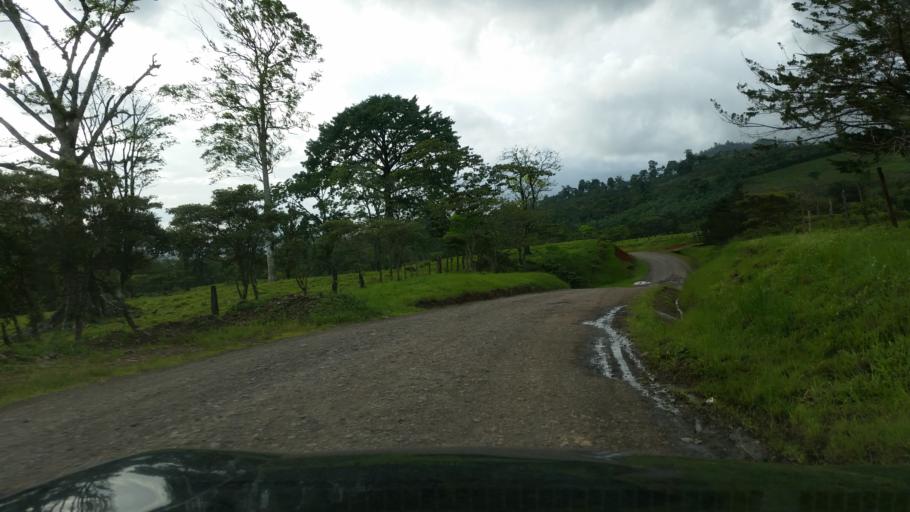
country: NI
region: Jinotega
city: Jinotega
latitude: 13.2688
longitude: -85.7311
